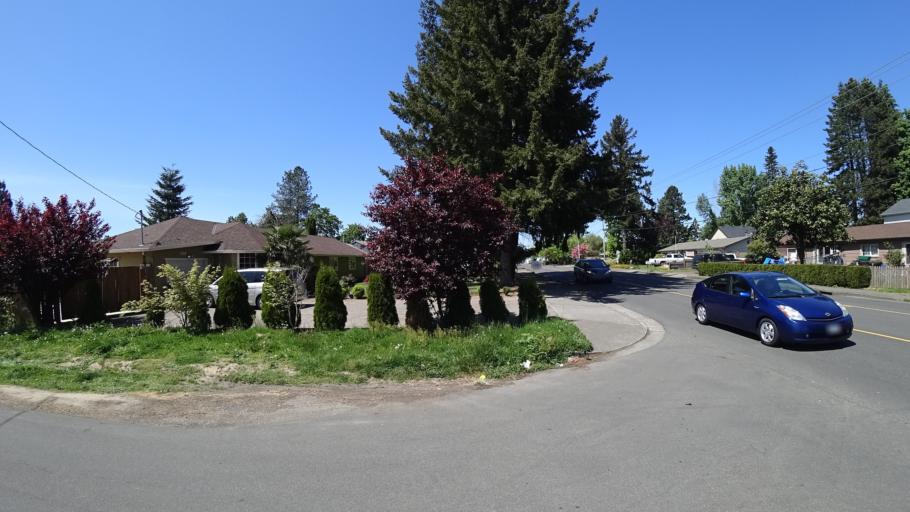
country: US
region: Oregon
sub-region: Washington County
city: Hillsboro
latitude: 45.5058
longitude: -122.9649
